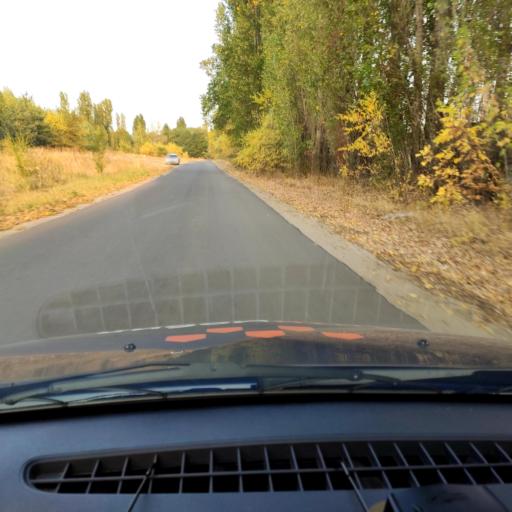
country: RU
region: Voronezj
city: Pridonskoy
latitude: 51.6646
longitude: 39.1174
